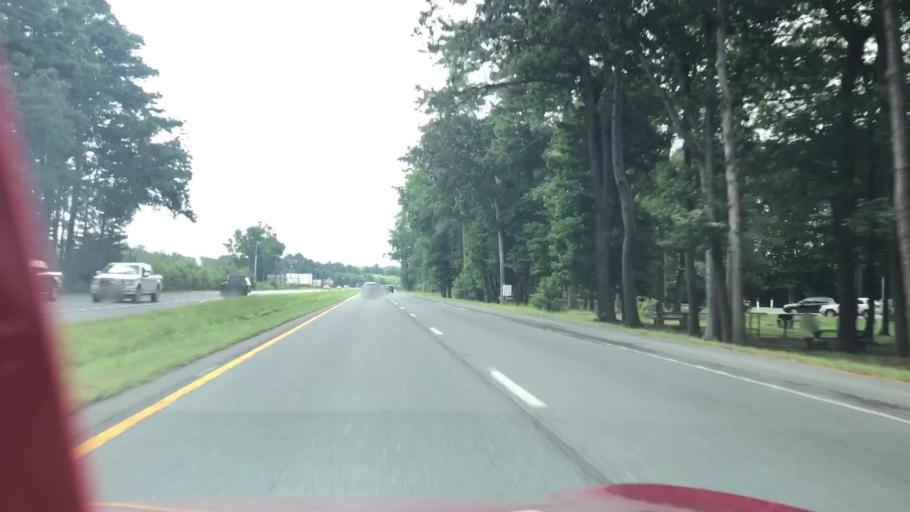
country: US
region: Virginia
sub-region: Accomack County
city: Wattsville
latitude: 37.9898
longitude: -75.5338
